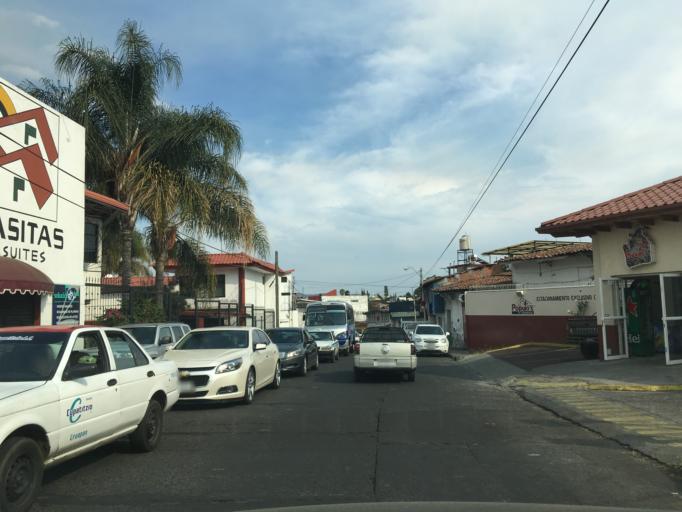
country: MX
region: Michoacan
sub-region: Uruapan
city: Uruapan
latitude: 19.4177
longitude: -102.0603
